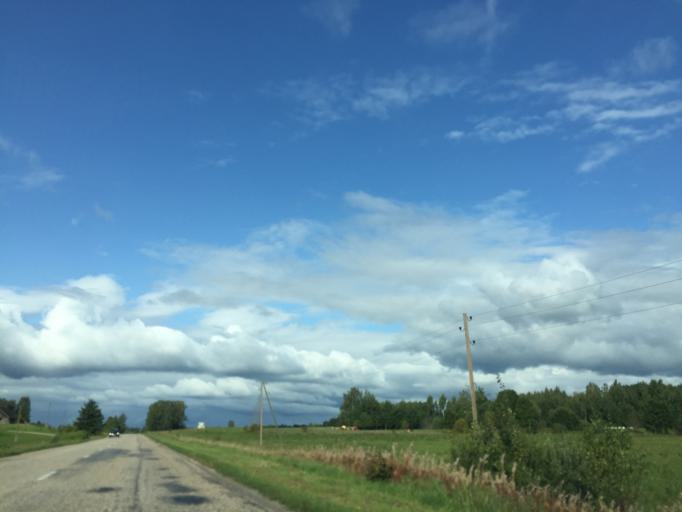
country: LV
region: Pargaujas
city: Stalbe
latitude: 57.4168
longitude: 24.9430
